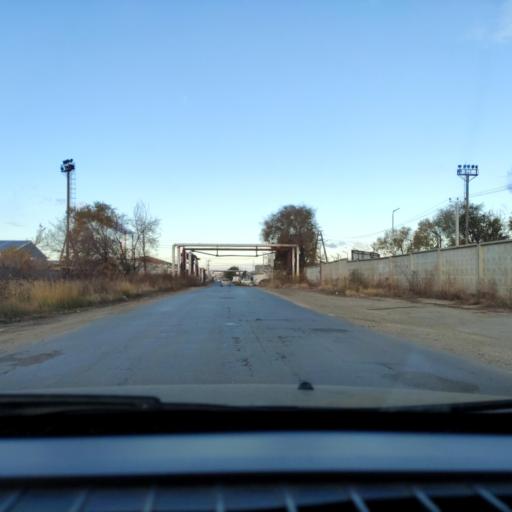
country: RU
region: Samara
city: Tol'yatti
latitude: 53.5752
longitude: 49.2854
